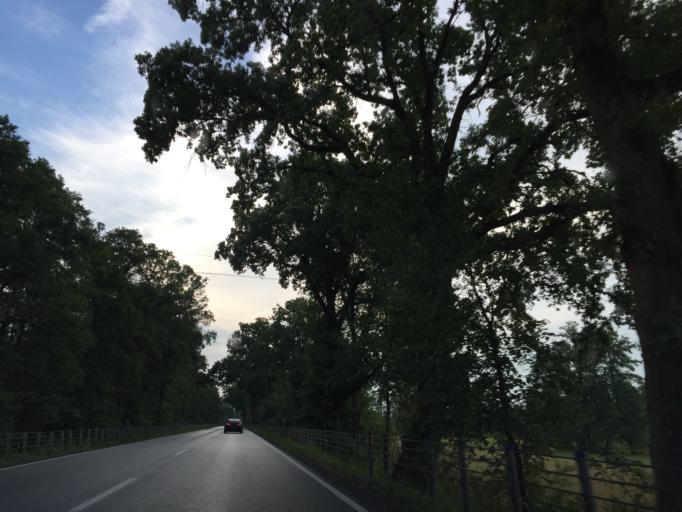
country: PL
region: Masovian Voivodeship
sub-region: Powiat wegrowski
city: Sadowne
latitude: 52.6612
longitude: 21.8482
